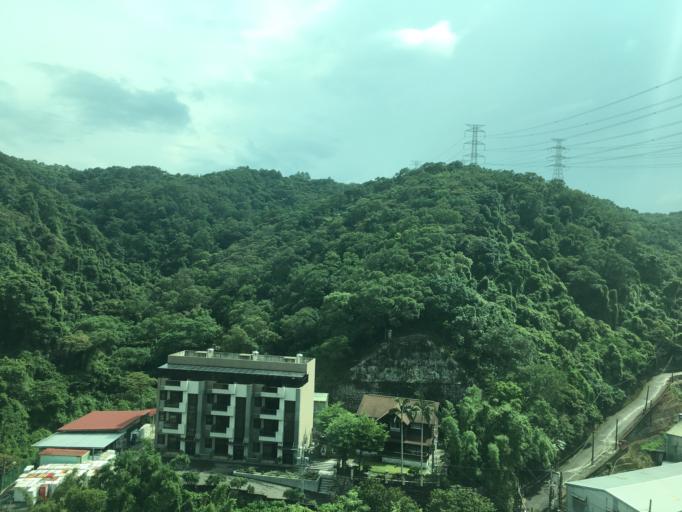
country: TW
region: Taipei
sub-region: Taipei
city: Banqiao
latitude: 25.0317
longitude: 121.3978
